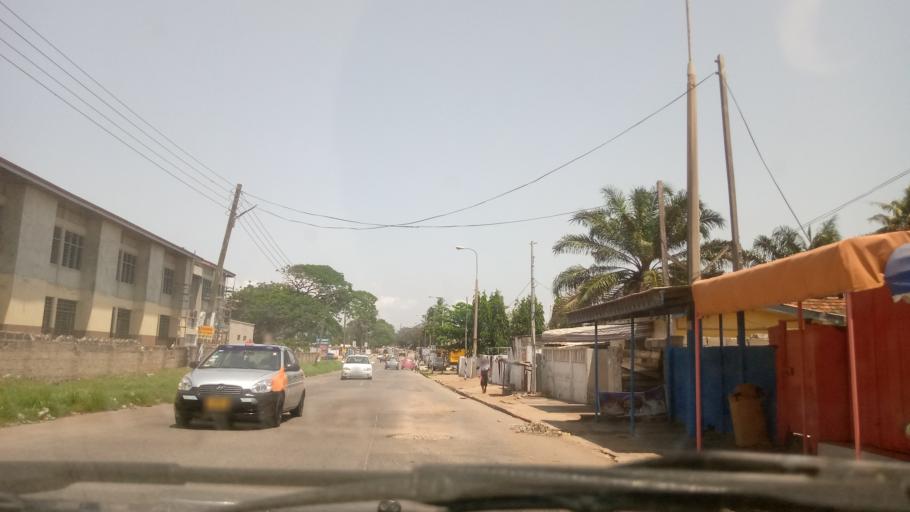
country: GH
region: Greater Accra
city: Accra
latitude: 5.5377
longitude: -0.2385
